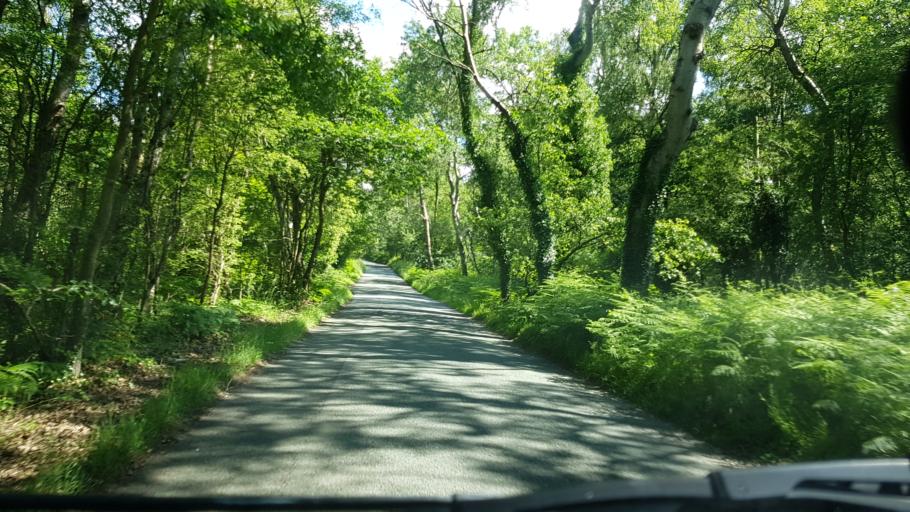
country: GB
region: England
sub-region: Worcestershire
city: Kidderminster
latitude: 52.4458
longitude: -2.2520
